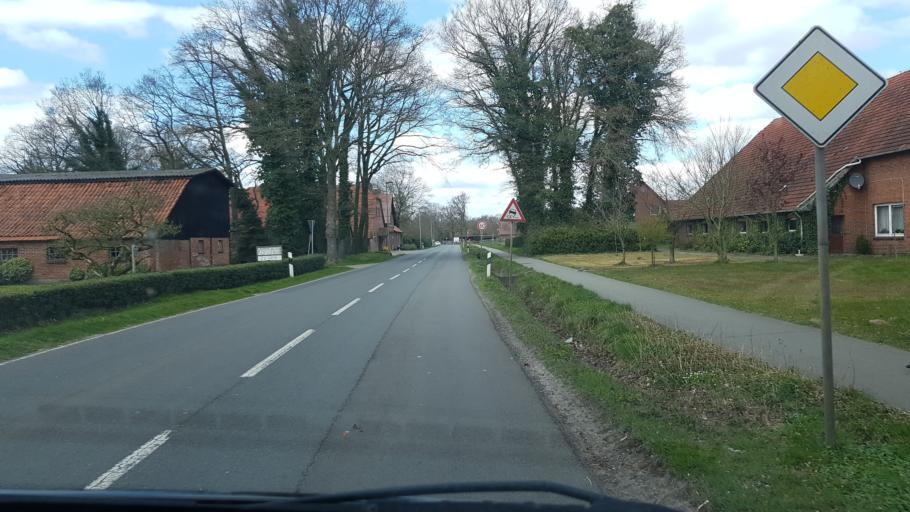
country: DE
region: Lower Saxony
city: Edewecht
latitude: 53.1188
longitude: 7.9422
